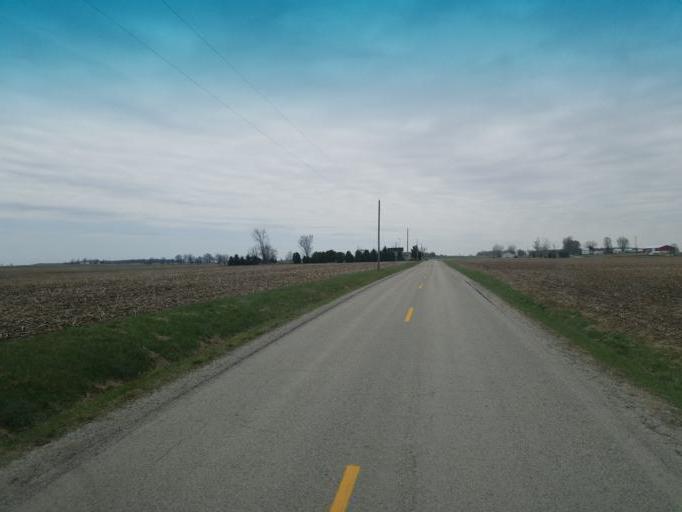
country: US
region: Ohio
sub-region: Crawford County
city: Bucyrus
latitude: 40.8562
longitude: -82.9355
